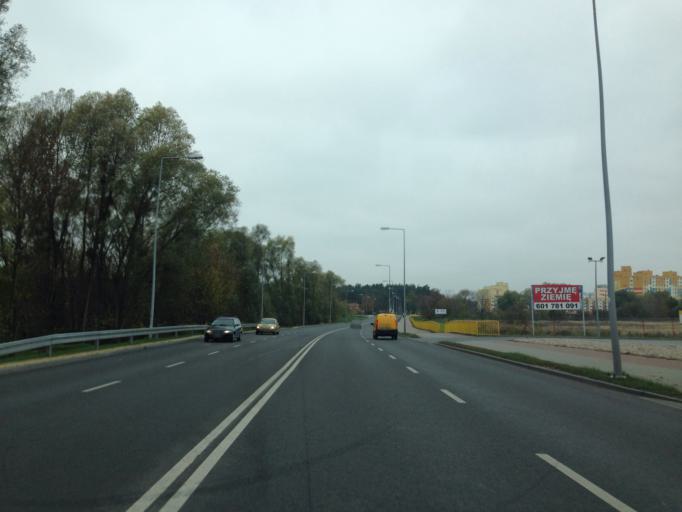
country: PL
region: Kujawsko-Pomorskie
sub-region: Grudziadz
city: Grudziadz
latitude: 53.4579
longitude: 18.7801
